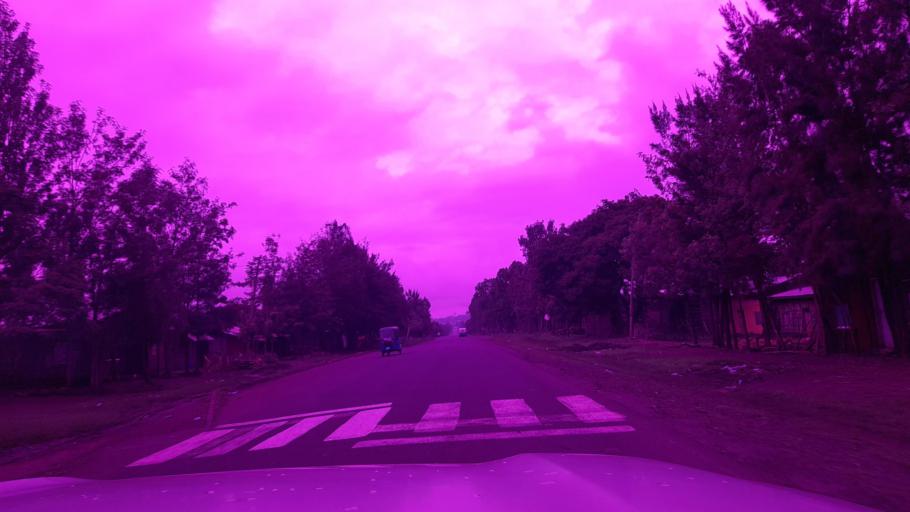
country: ET
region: Oromiya
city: Waliso
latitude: 8.2809
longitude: 37.6877
